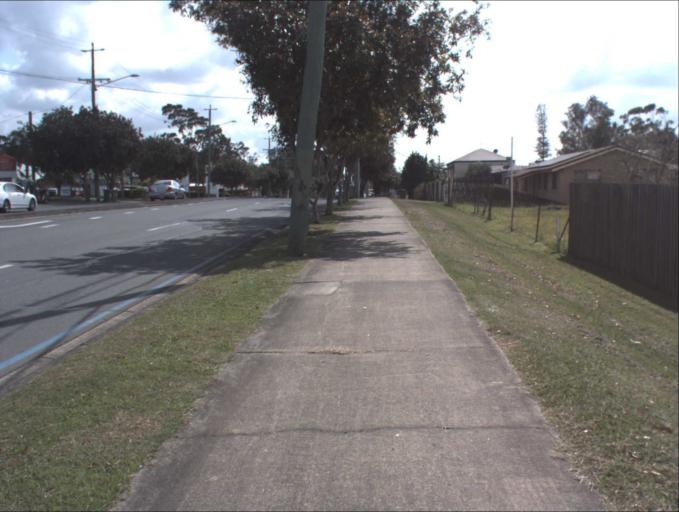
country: AU
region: Queensland
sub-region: Logan
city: Waterford West
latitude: -27.6897
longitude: 153.1368
